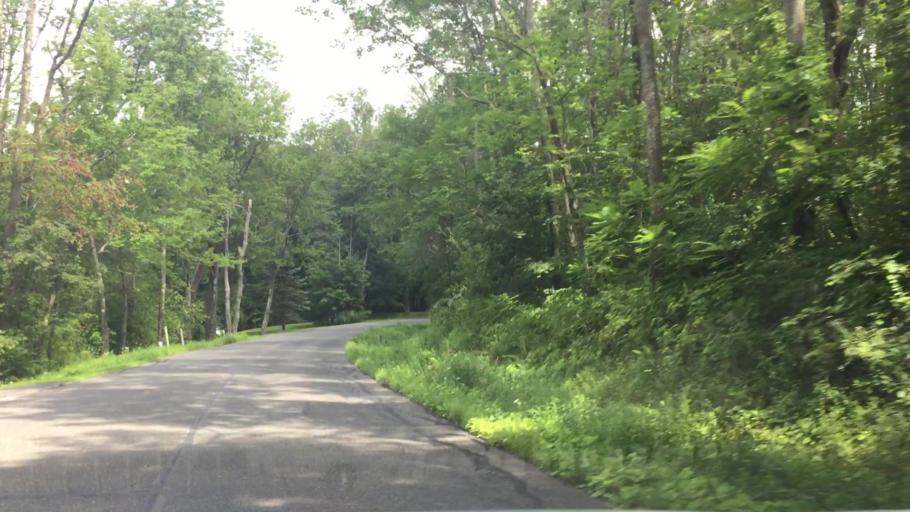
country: US
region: Massachusetts
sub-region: Berkshire County
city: Lee
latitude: 42.2726
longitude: -73.1989
